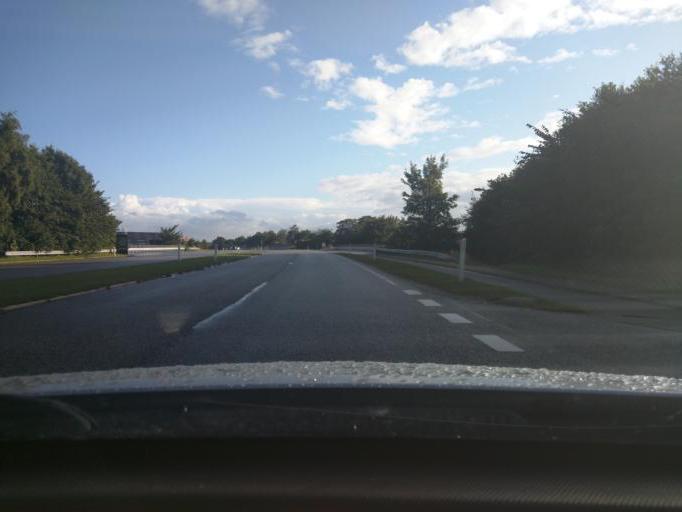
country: DK
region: Central Jutland
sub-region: Viborg Kommune
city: Viborg
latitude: 56.4675
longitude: 9.4127
